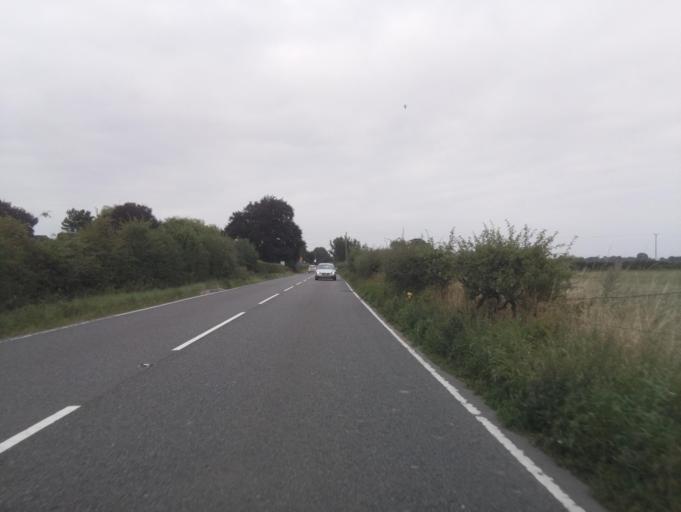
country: GB
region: England
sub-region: Shropshire
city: Astley
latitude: 52.7563
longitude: -2.6960
